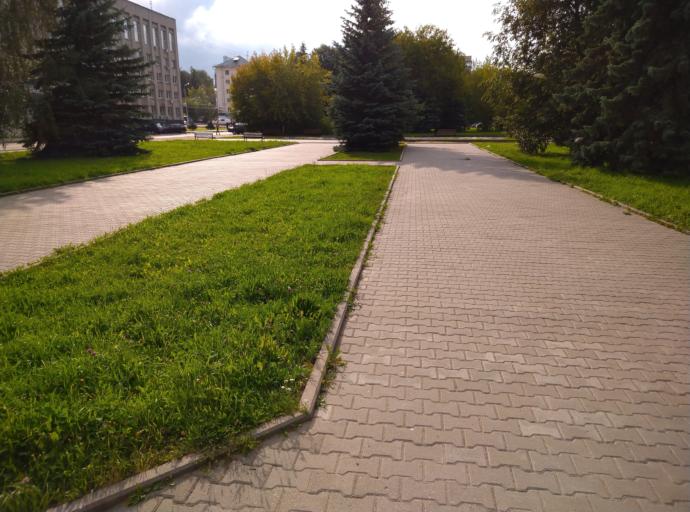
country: RU
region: Kostroma
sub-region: Kostromskoy Rayon
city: Kostroma
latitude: 57.7588
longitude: 40.9636
